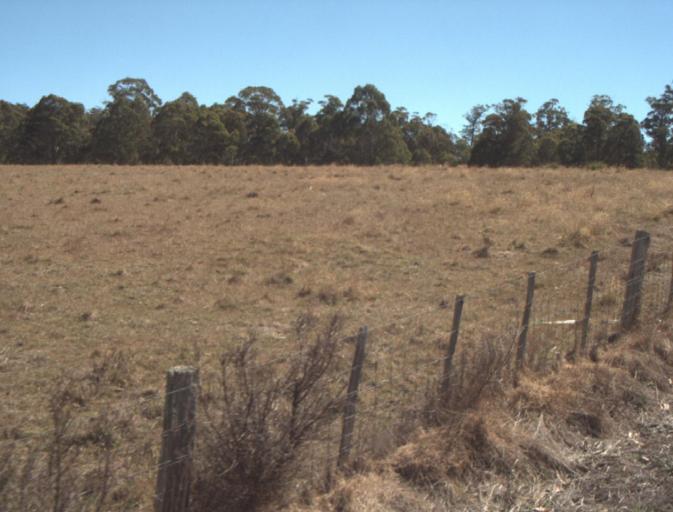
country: AU
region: Tasmania
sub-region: Launceston
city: Newstead
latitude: -41.3160
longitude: 147.3311
